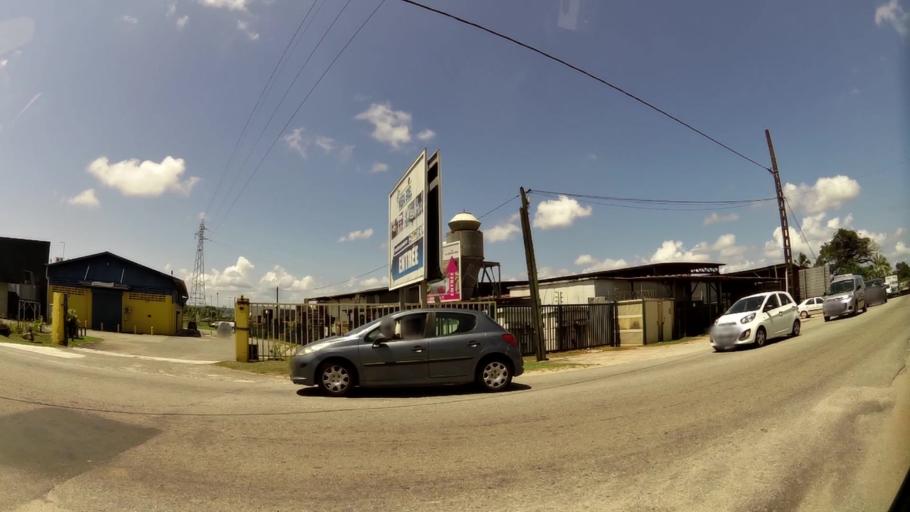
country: GF
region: Guyane
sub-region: Guyane
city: Cayenne
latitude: 4.9075
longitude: -52.3238
